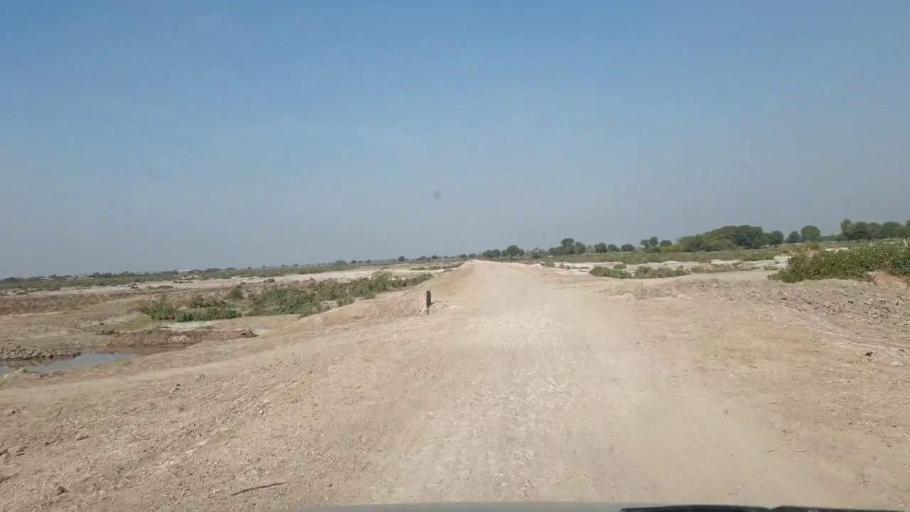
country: PK
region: Sindh
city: Chambar
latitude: 25.3259
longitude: 68.8098
